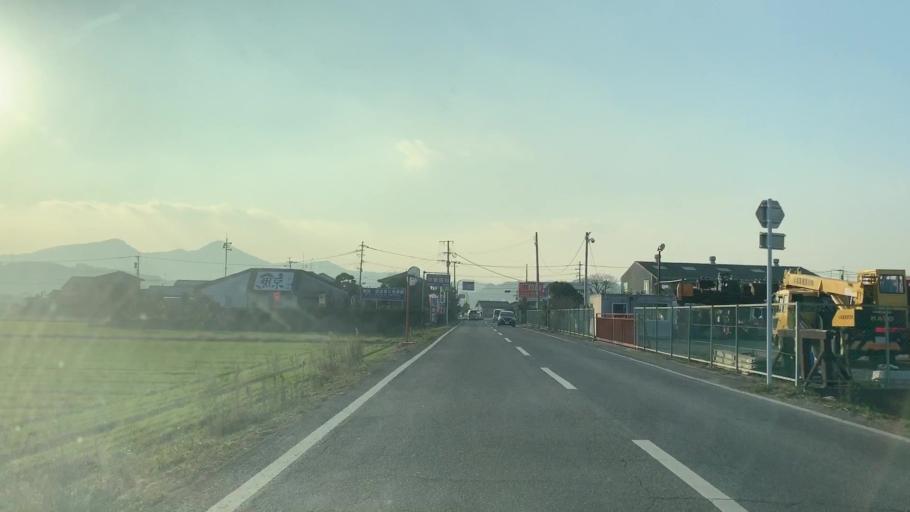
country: JP
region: Saga Prefecture
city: Saga-shi
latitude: 33.2749
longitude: 130.2023
